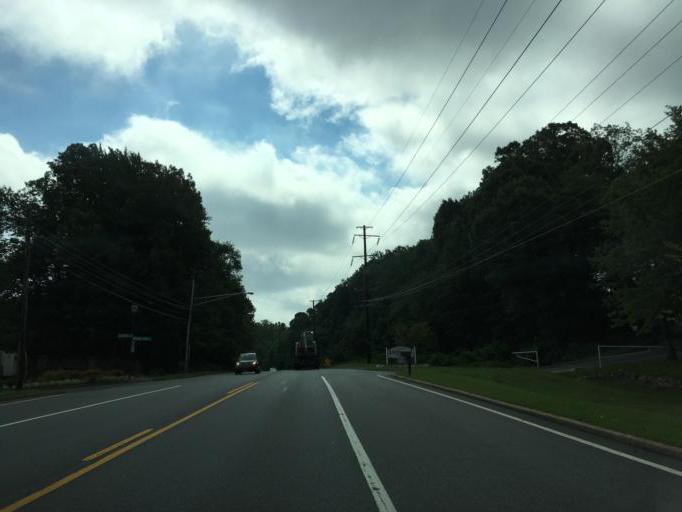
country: US
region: Maryland
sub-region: Anne Arundel County
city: Crownsville
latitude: 39.0169
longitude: -76.5803
